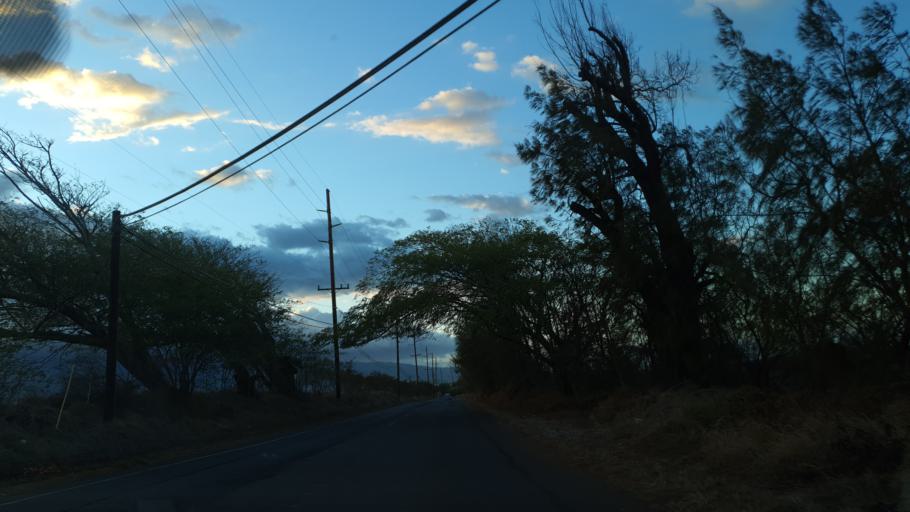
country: US
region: Hawaii
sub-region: Maui County
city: Kahului
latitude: 20.8679
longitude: -156.4347
